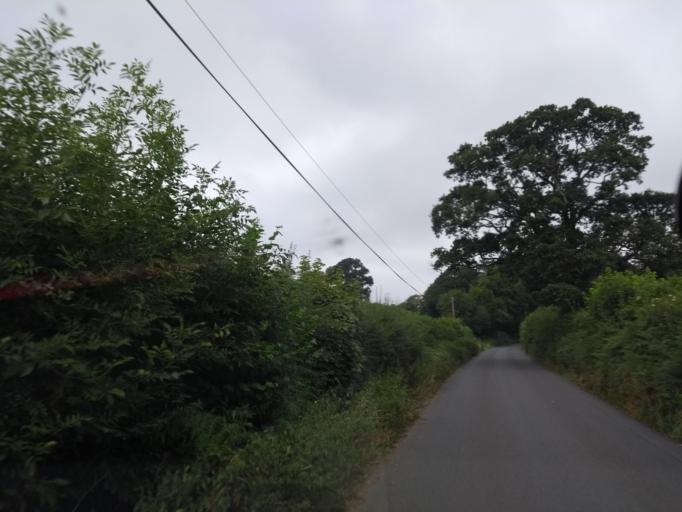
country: GB
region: England
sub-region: Somerset
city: Chard
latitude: 50.8763
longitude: -3.0812
